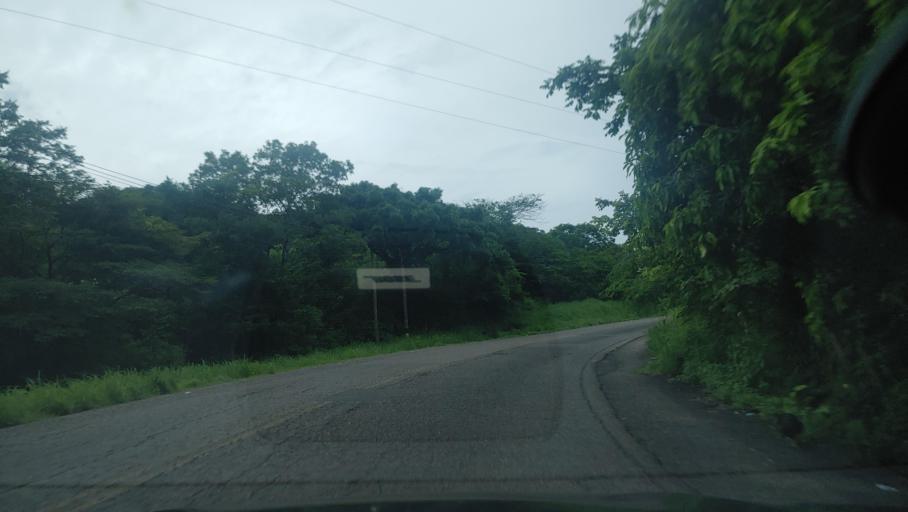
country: HN
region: Choluteca
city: Corpus
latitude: 13.3762
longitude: -87.0556
